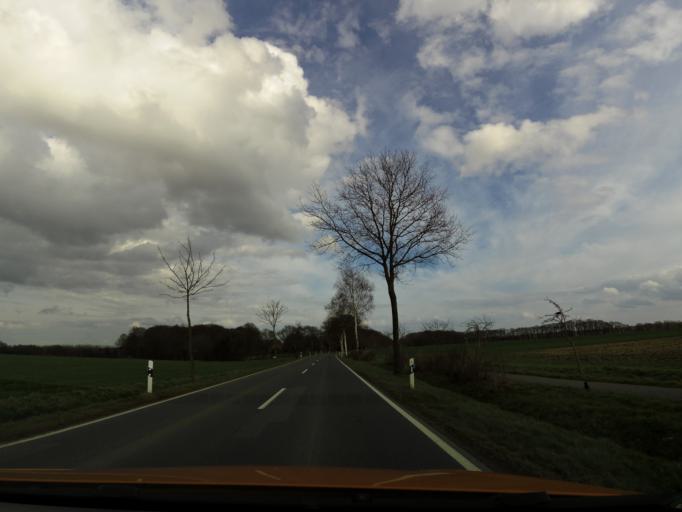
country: DE
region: Lower Saxony
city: Bruchhausen-Vilsen
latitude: 52.8265
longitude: 8.9571
